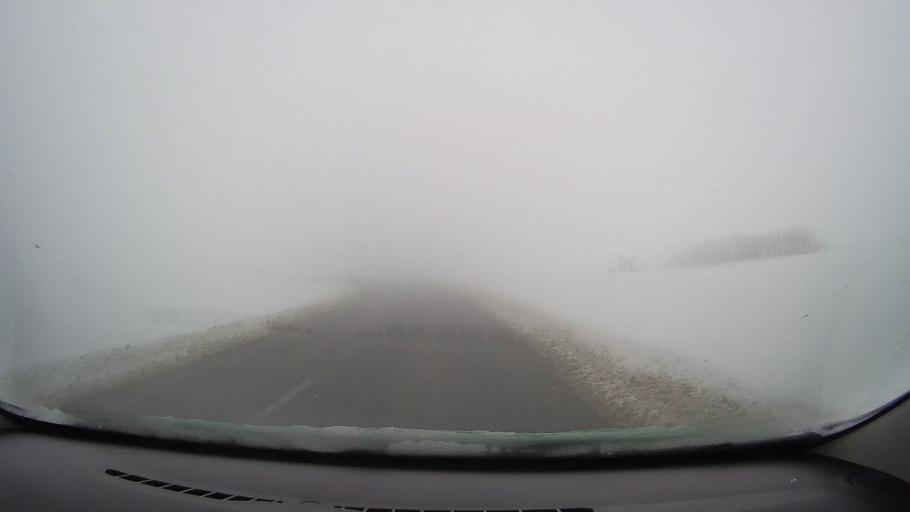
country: RO
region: Sibiu
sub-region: Comuna Poiana Sibiului
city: Poiana Sibiului
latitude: 45.7968
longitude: 23.7076
